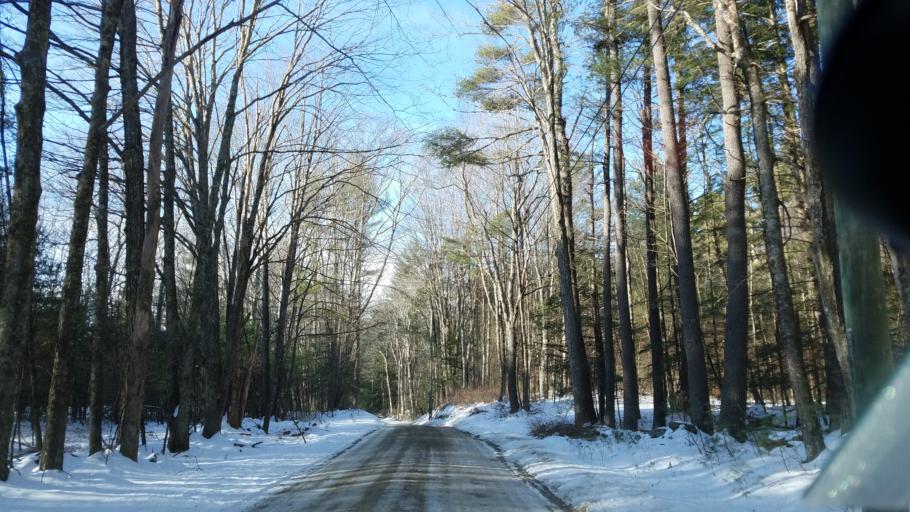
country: US
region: Massachusetts
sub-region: Hampden County
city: Holland
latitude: 41.9660
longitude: -72.0932
